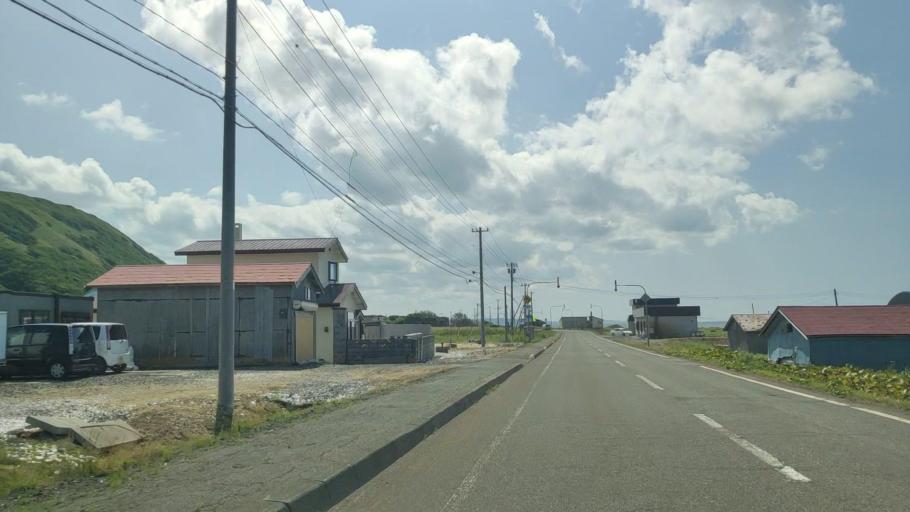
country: JP
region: Hokkaido
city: Wakkanai
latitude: 45.4069
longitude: 141.6362
